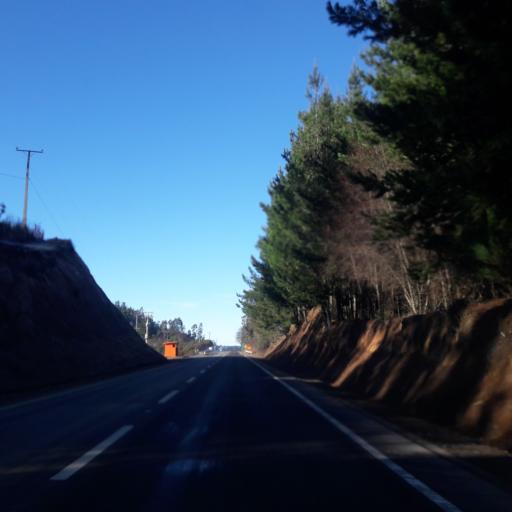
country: CL
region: Biobio
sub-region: Provincia de Biobio
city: La Laja
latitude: -37.3010
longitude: -72.9281
